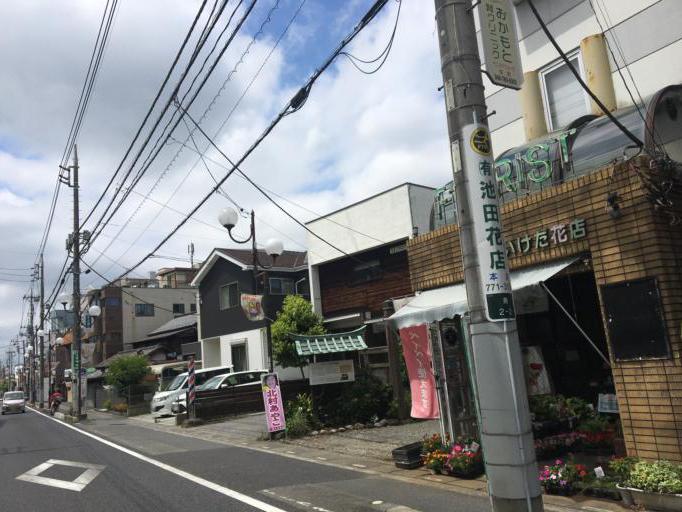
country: JP
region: Saitama
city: Okegawa
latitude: 36.0016
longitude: 139.5649
